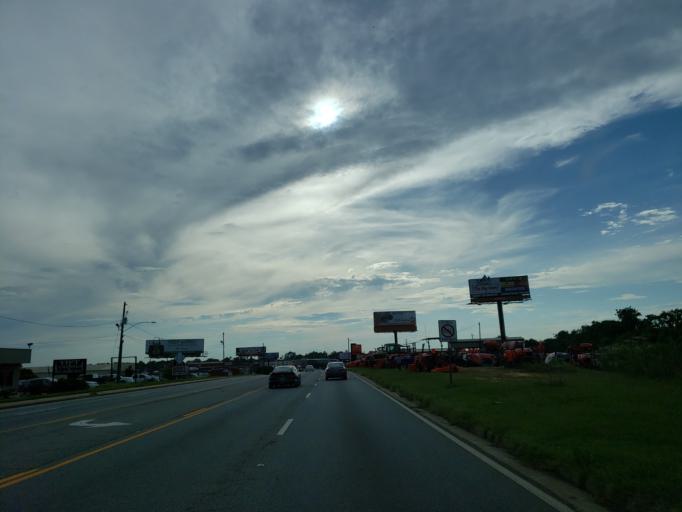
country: US
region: Georgia
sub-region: Tift County
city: Tifton
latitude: 31.4505
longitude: -83.5021
